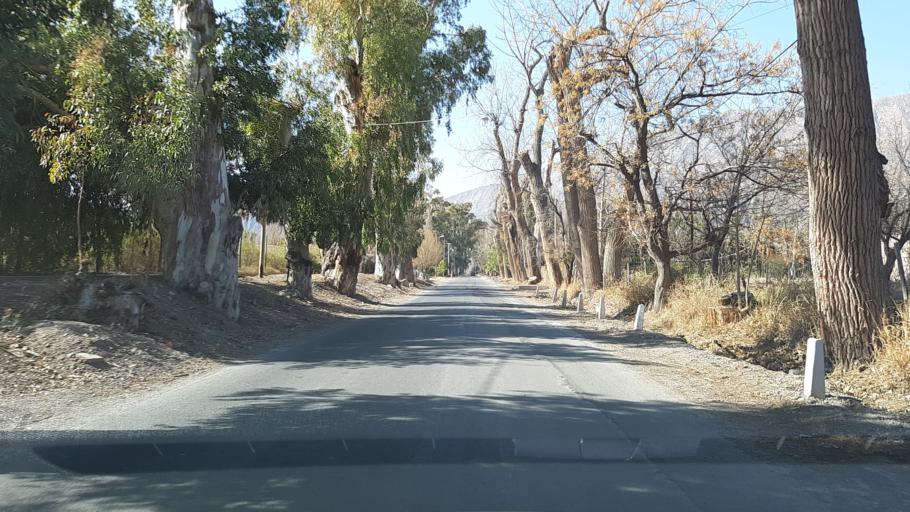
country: AR
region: San Juan
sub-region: Departamento de Zonda
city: Zonda
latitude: -31.5607
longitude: -68.7273
